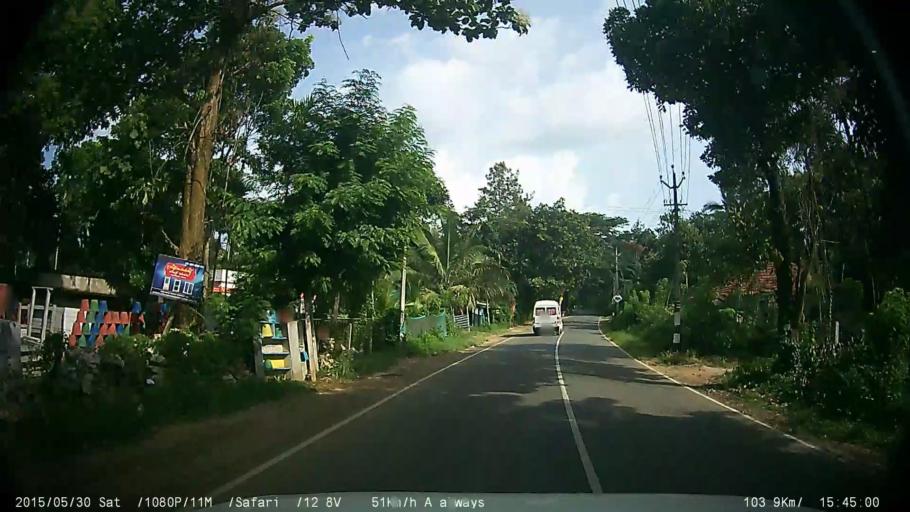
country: IN
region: Kerala
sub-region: Wayanad
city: Panamaram
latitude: 11.7208
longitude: 76.0801
